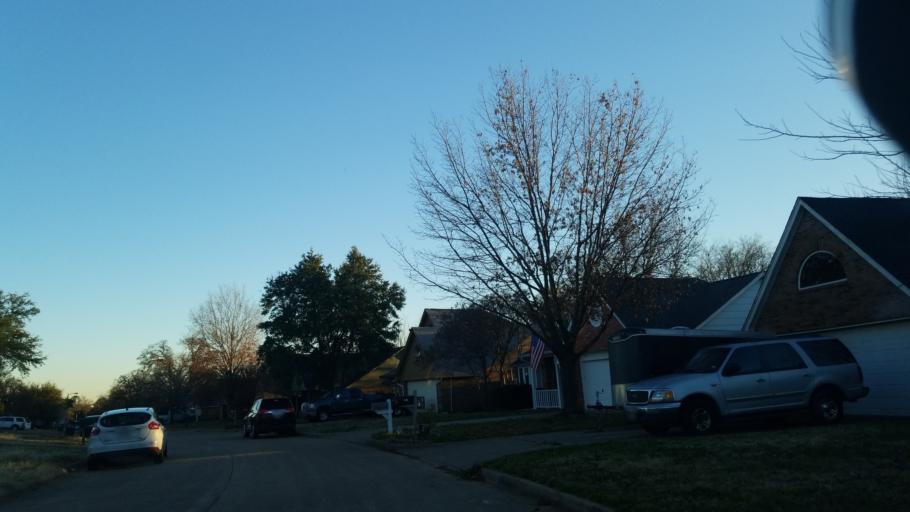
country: US
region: Texas
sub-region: Denton County
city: Corinth
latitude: 33.1393
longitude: -97.0538
